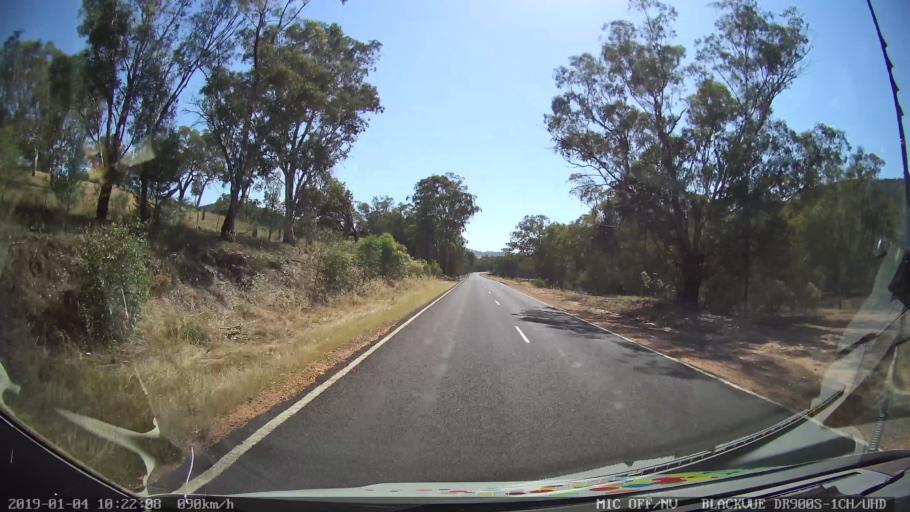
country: AU
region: New South Wales
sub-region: Cabonne
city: Canowindra
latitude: -33.3691
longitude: 148.5206
